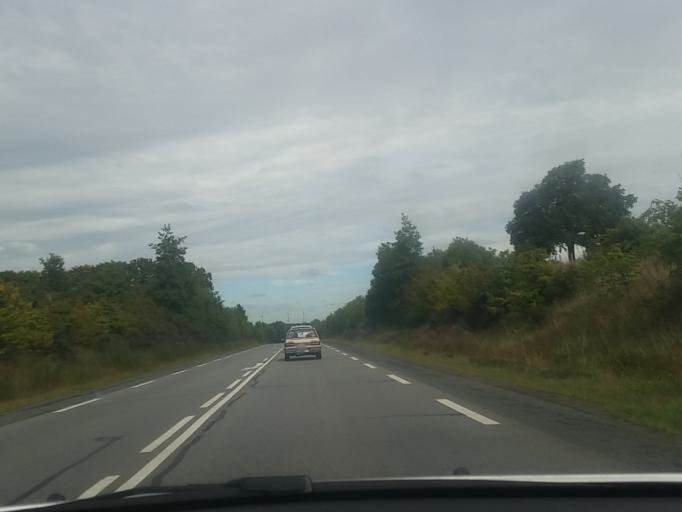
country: FR
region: Brittany
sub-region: Departement d'Ille-et-Vilaine
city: Martigne-Ferchaud
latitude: 47.8272
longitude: -1.3278
